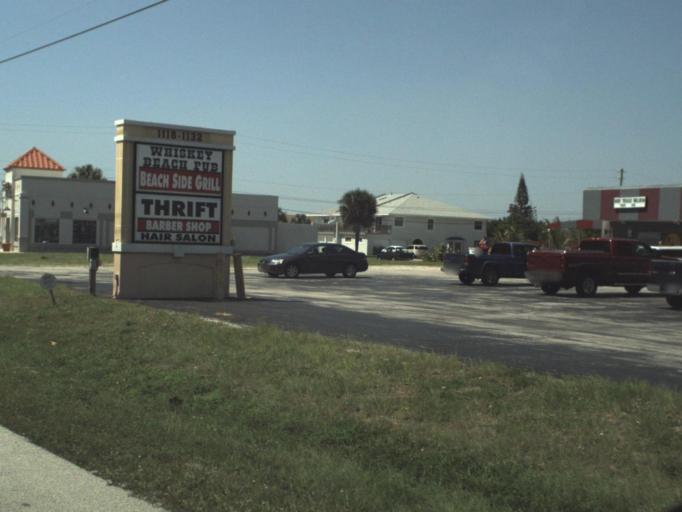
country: US
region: Florida
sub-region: Brevard County
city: Satellite Beach
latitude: 28.1824
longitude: -80.5921
